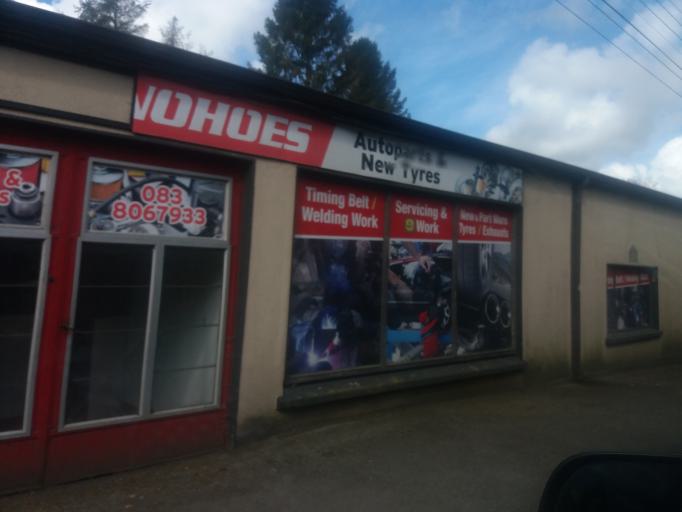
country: IE
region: Ulster
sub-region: An Cabhan
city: Cavan
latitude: 53.9847
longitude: -7.3592
